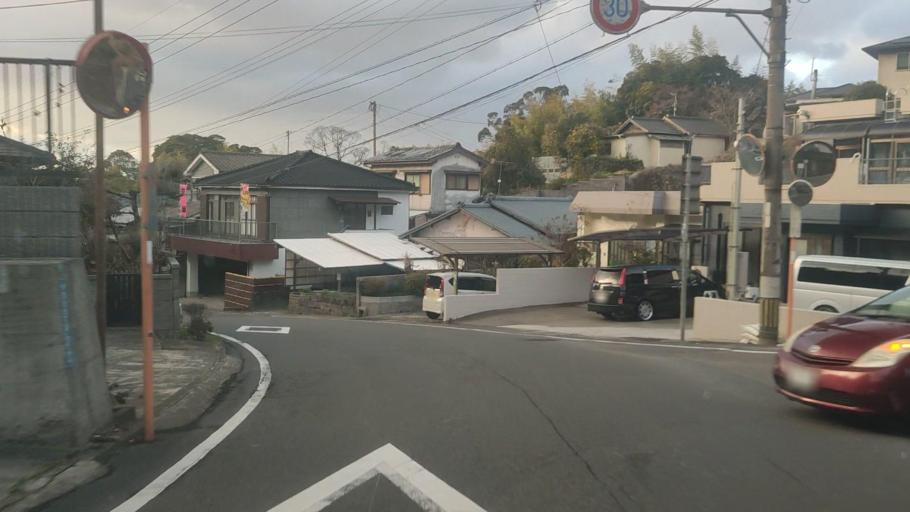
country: JP
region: Kagoshima
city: Kagoshima-shi
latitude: 31.6270
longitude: 130.5534
